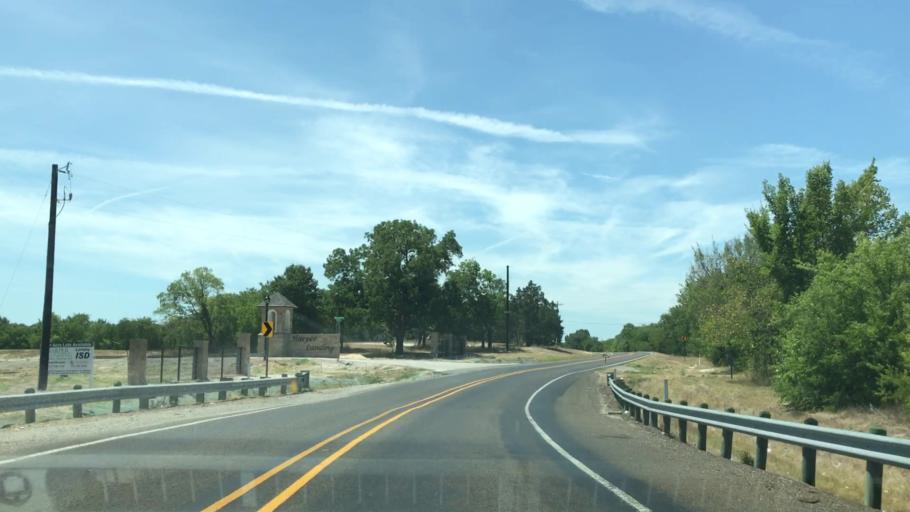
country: US
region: Texas
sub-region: Collin County
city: Fairview
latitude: 33.1408
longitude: -96.6070
